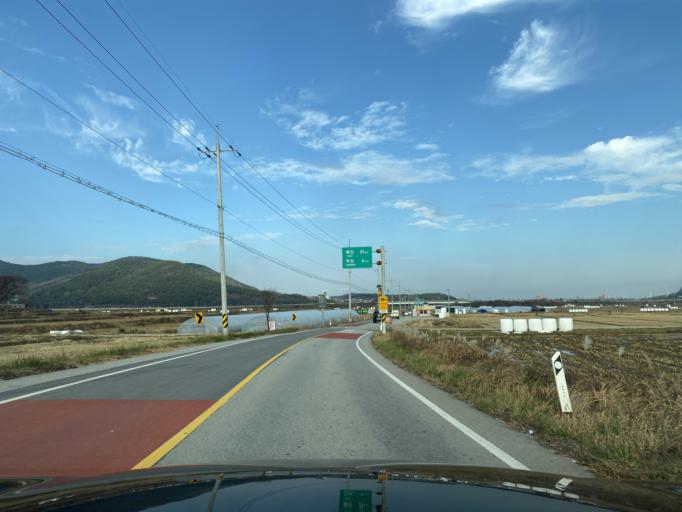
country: KR
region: Chungcheongnam-do
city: Hongsung
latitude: 36.6755
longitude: 126.6427
